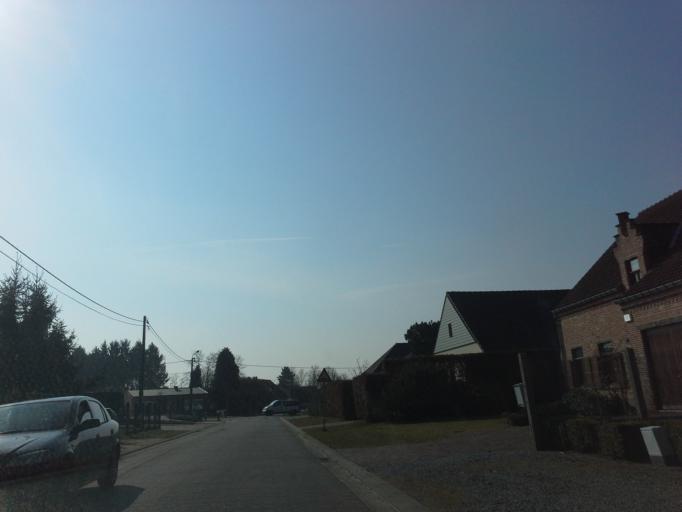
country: BE
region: Flanders
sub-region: Provincie Antwerpen
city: Meerhout
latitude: 51.1286
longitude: 5.0761
